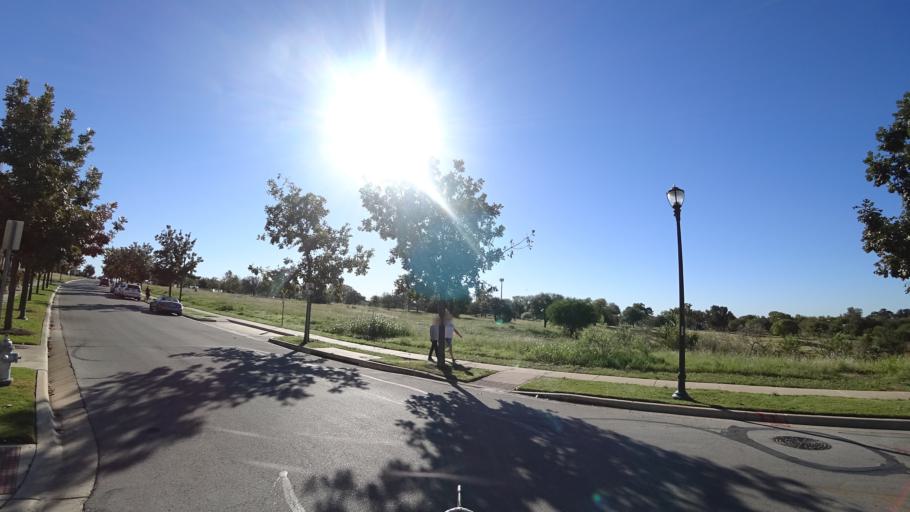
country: US
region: Texas
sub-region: Travis County
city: Austin
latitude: 30.2900
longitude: -97.7009
